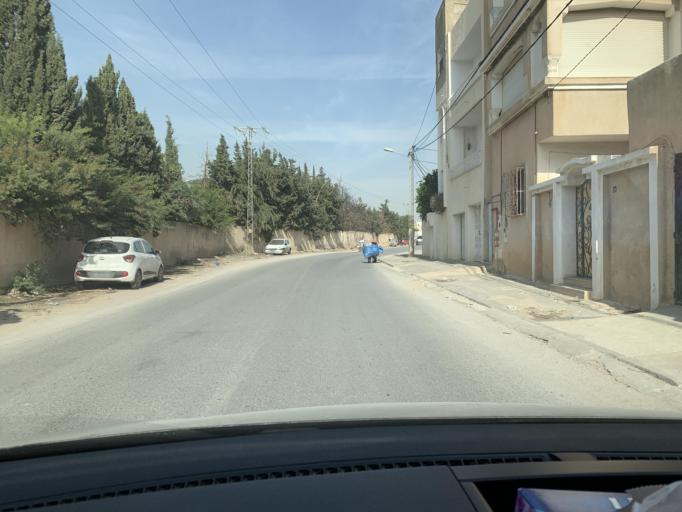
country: TN
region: Manouba
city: Manouba
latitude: 36.8157
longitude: 10.1172
